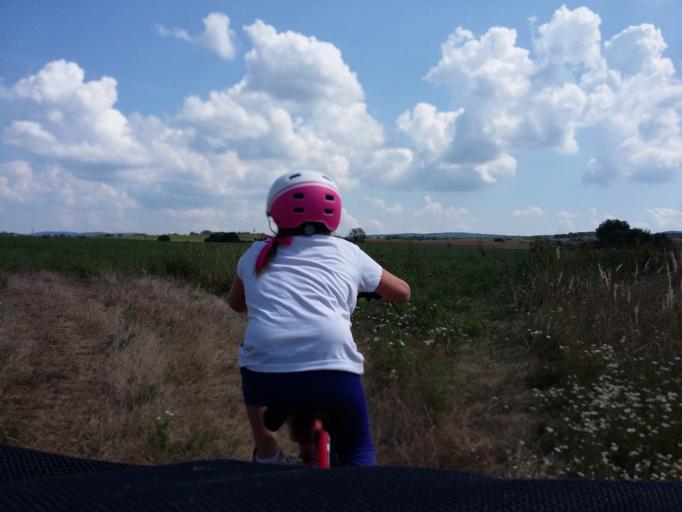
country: SK
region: Bratislavsky
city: Stupava
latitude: 48.3247
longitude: 17.0393
